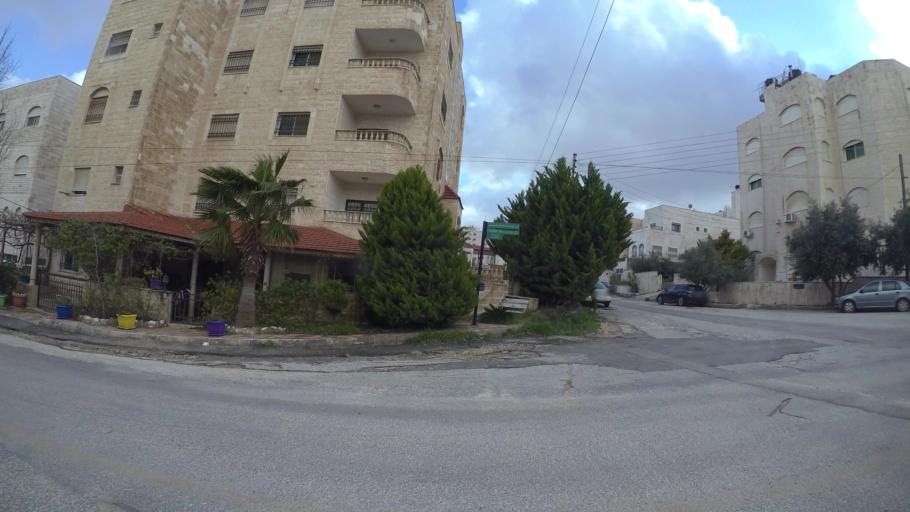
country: JO
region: Amman
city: Al Jubayhah
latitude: 32.0526
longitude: 35.8918
